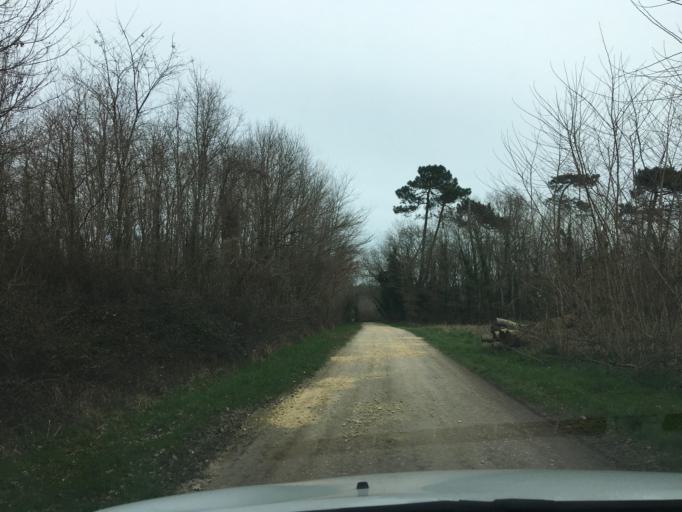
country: FR
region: Aquitaine
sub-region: Departement de la Gironde
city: Saint-Sauveur
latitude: 45.2221
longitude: -0.8644
